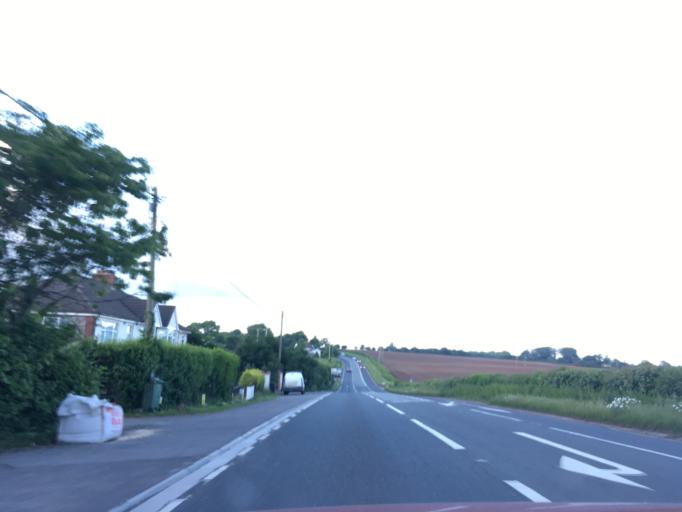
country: GB
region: England
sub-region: North Somerset
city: Butcombe
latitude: 51.3714
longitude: -2.7126
